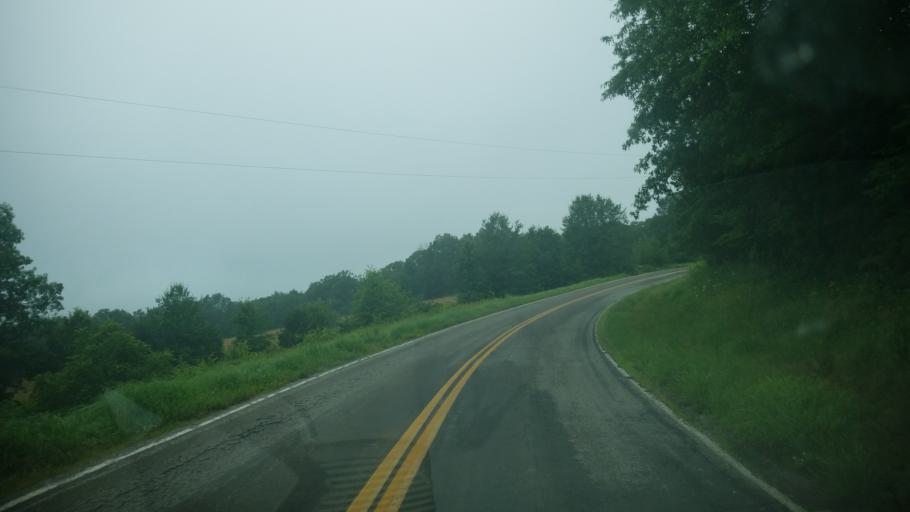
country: US
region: Missouri
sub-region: Audrain County
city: Vandalia
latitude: 39.2880
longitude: -91.3502
